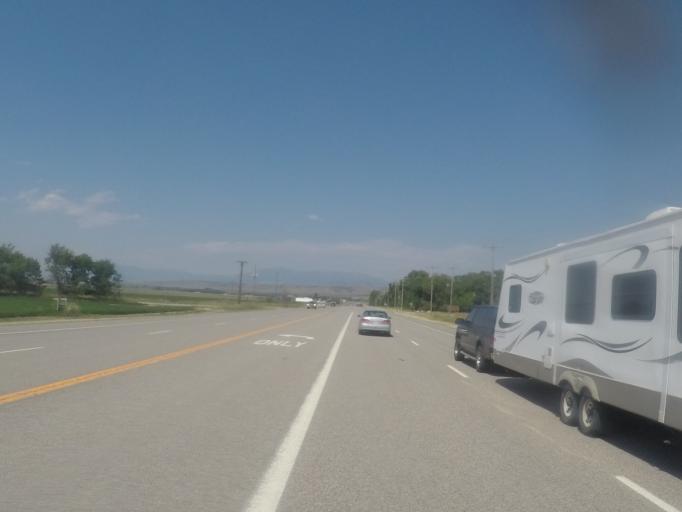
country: US
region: Montana
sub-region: Broadwater County
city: Townsend
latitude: 46.1506
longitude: -111.4676
